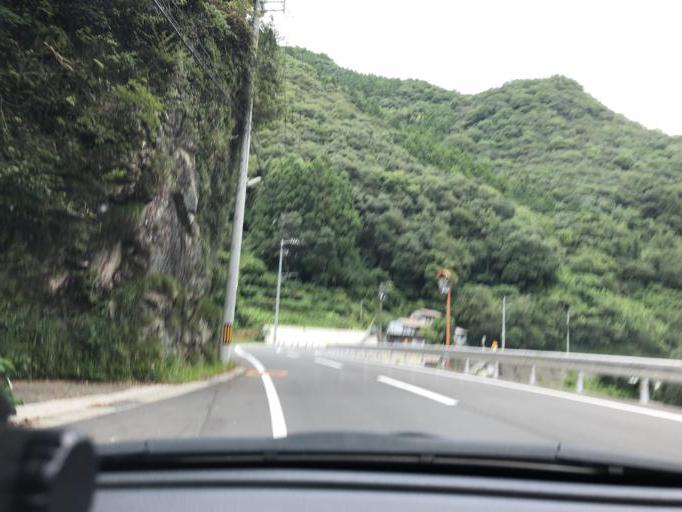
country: JP
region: Kochi
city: Kochi-shi
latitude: 33.6248
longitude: 133.4989
